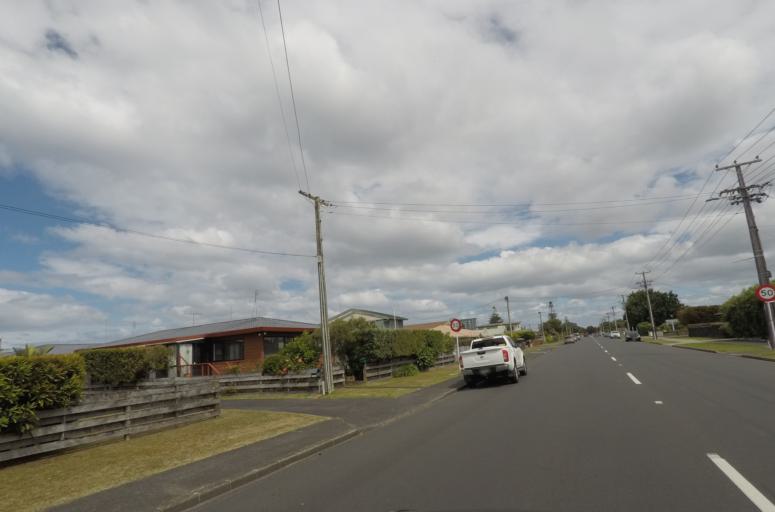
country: NZ
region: Auckland
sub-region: Auckland
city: Rothesay Bay
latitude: -36.5828
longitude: 174.6901
